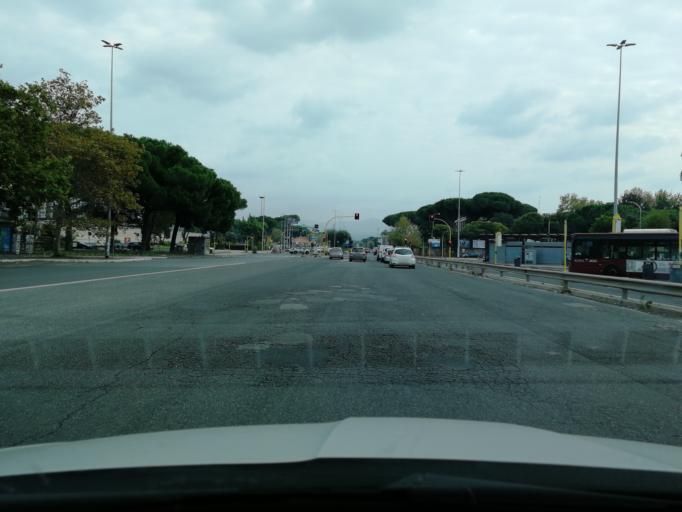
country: IT
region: Latium
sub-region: Citta metropolitana di Roma Capitale
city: Ciampino
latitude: 41.8531
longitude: 12.5687
